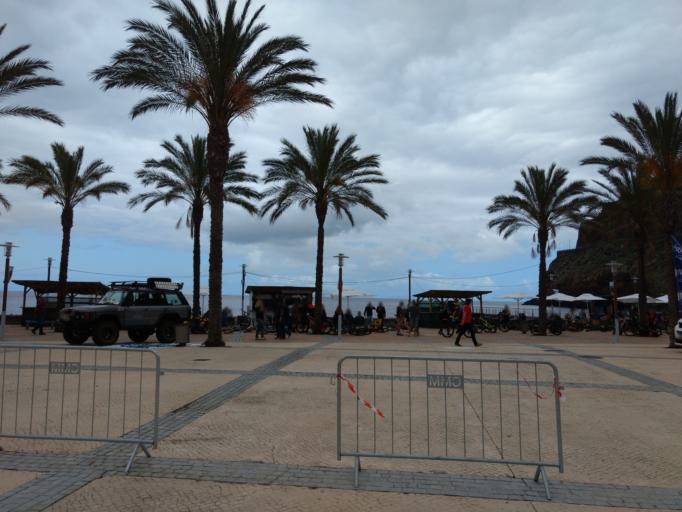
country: PT
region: Madeira
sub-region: Machico
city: Machico
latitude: 32.7169
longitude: -16.7650
